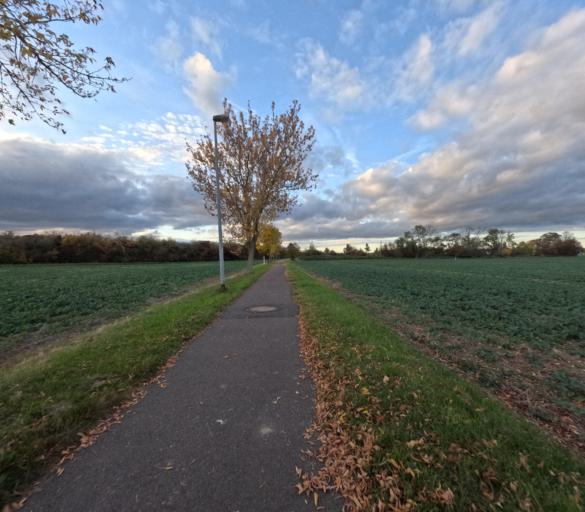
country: DE
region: Saxony
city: Naunhof
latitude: 51.2588
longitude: 12.6249
